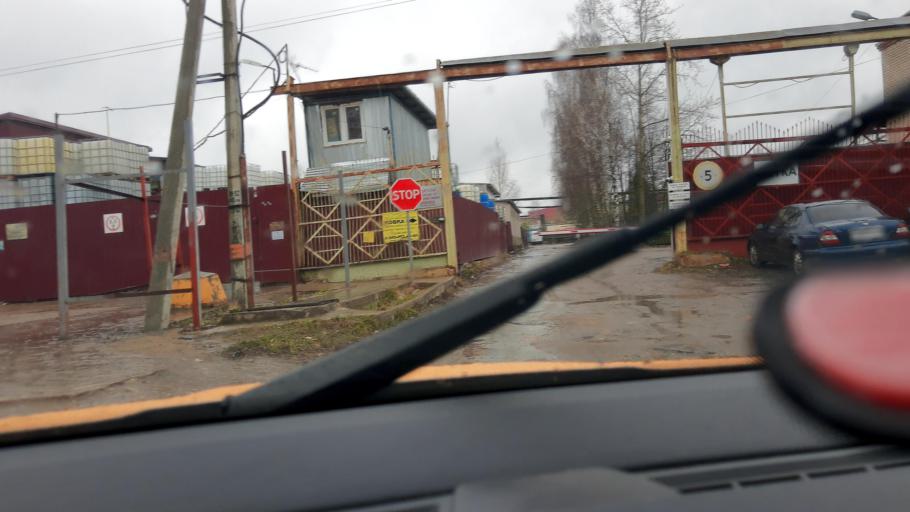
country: RU
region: Moskovskaya
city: Lesnoy
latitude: 56.0716
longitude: 37.9264
